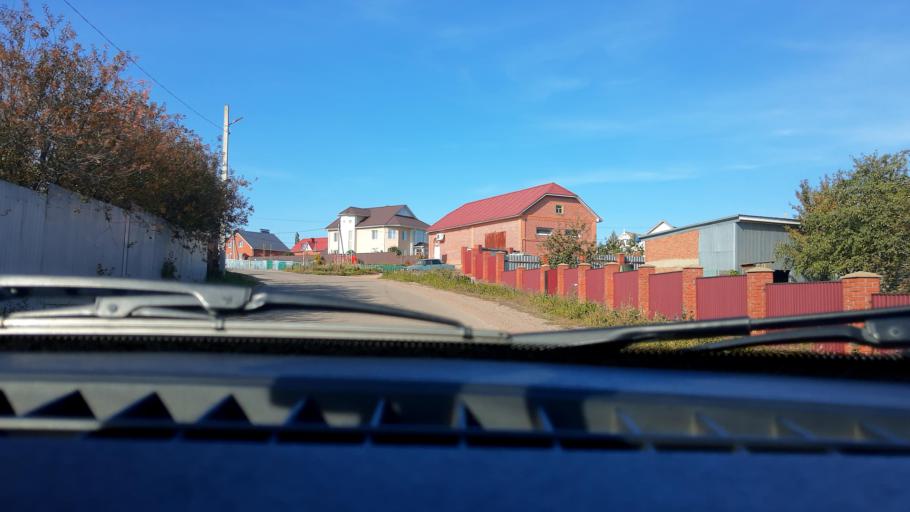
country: RU
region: Bashkortostan
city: Mikhaylovka
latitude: 54.8145
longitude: 55.8925
